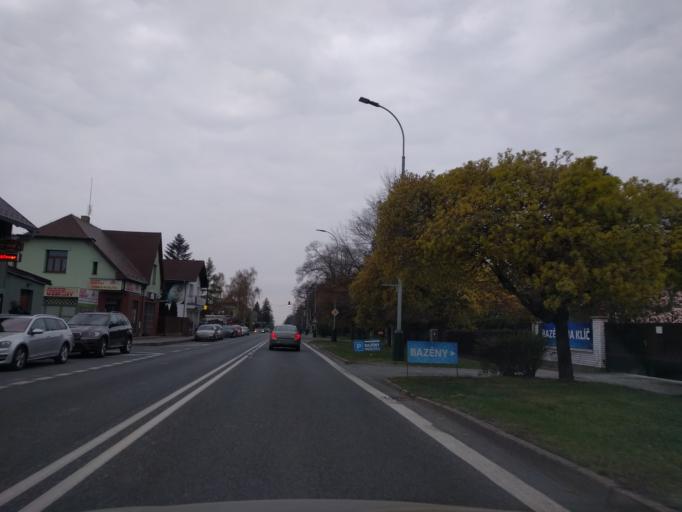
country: CZ
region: Central Bohemia
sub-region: Okres Praha-Vychod
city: Ricany
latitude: 49.9940
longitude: 14.6851
